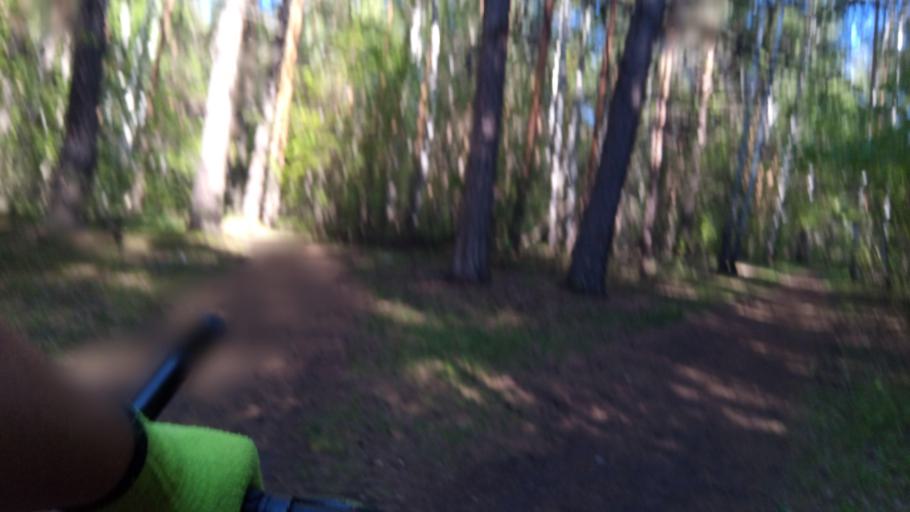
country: RU
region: Chelyabinsk
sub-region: Gorod Chelyabinsk
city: Chelyabinsk
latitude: 55.1481
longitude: 61.3456
